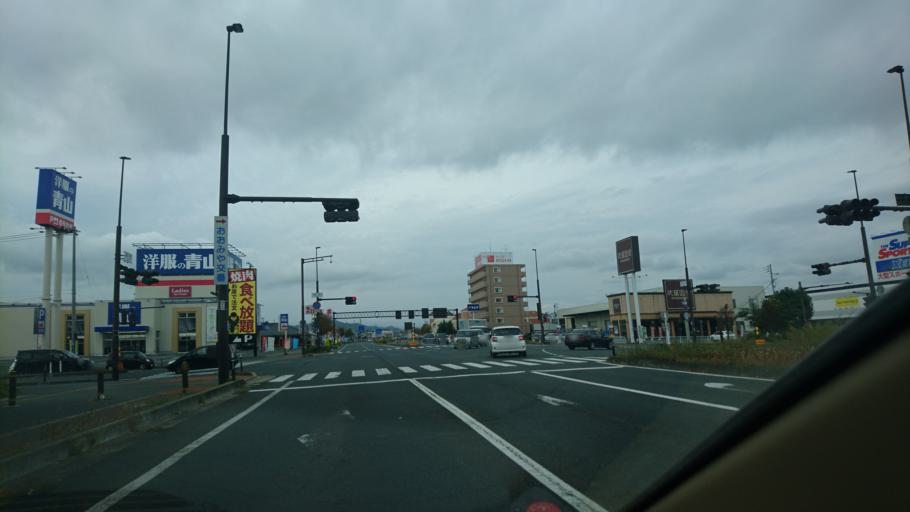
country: JP
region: Iwate
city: Morioka-shi
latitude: 39.6850
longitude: 141.1270
